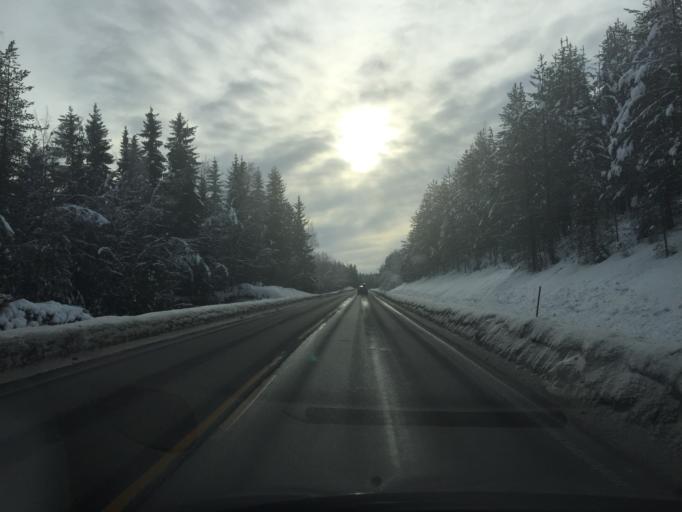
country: NO
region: Hedmark
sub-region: Trysil
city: Innbygda
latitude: 61.2675
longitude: 12.3058
